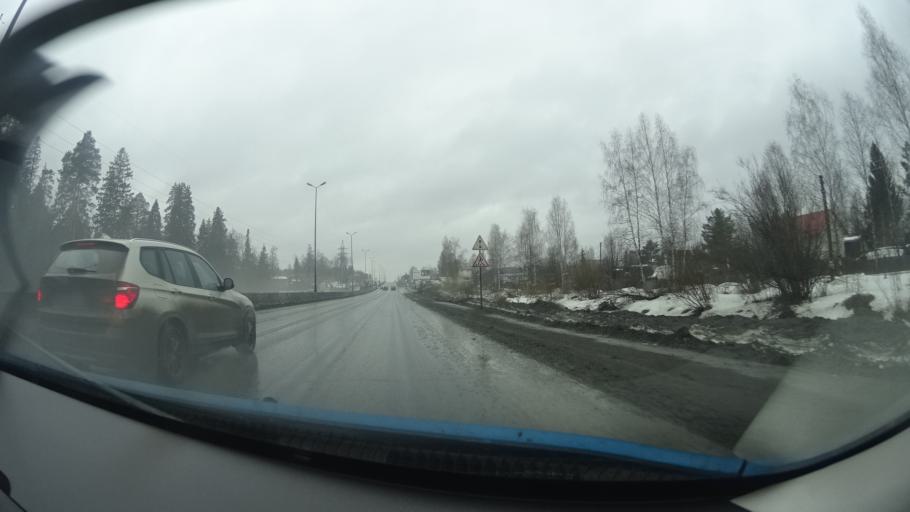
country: RU
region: Perm
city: Kondratovo
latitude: 58.0546
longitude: 56.1267
